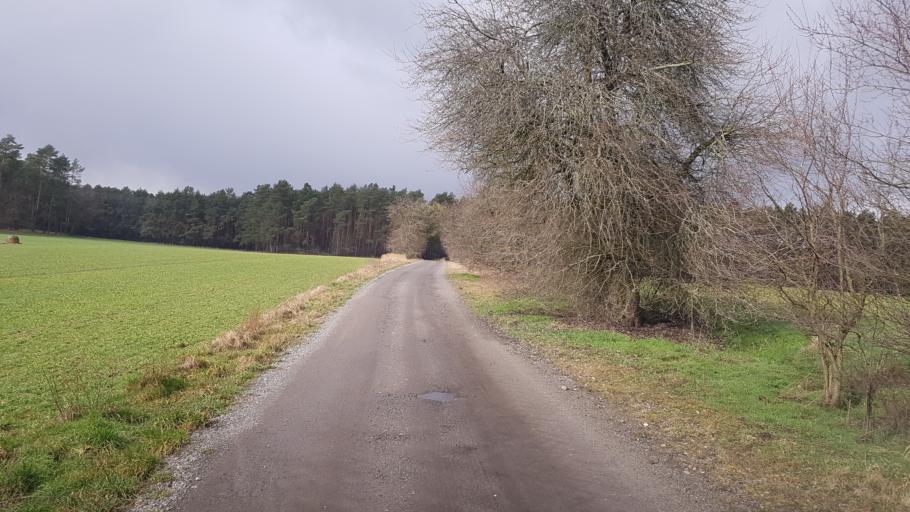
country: DE
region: Brandenburg
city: Sallgast
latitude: 51.6537
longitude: 13.8481
